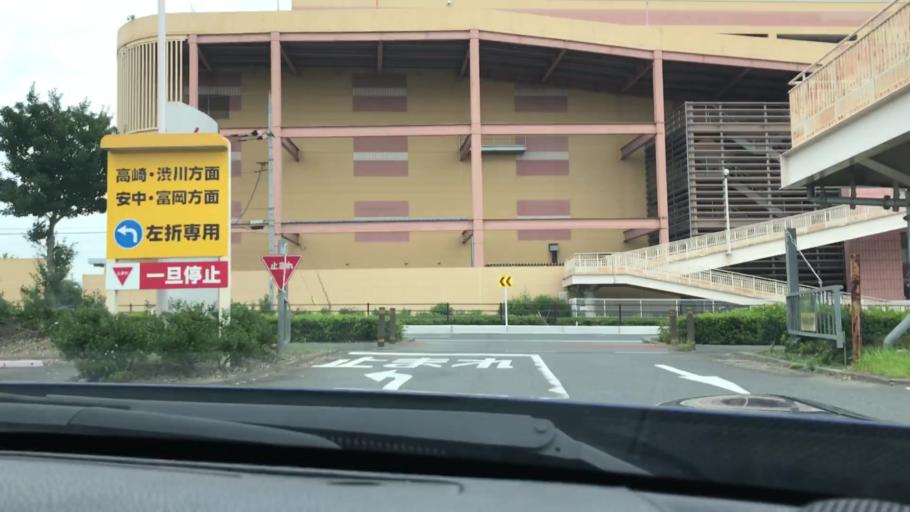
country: JP
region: Gunma
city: Kanekomachi
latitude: 36.3884
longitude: 139.0068
